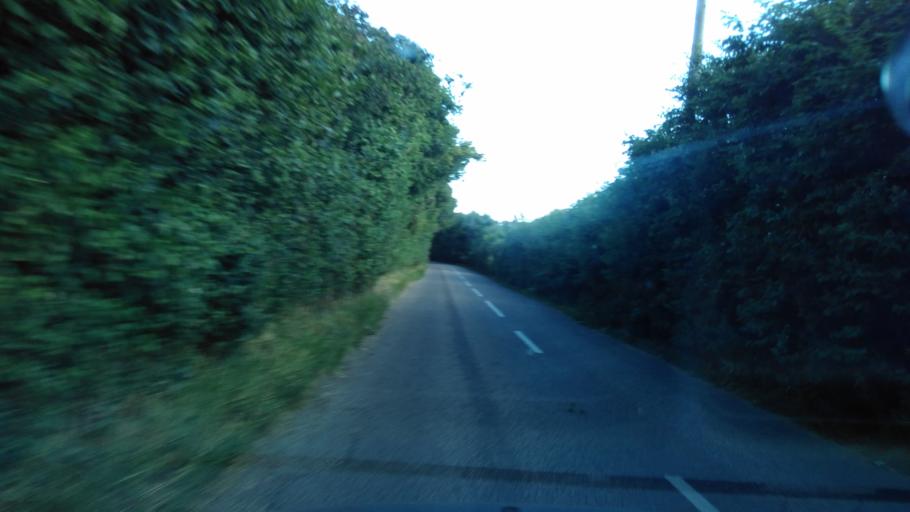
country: GB
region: England
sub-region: Kent
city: Dunkirk
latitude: 51.2541
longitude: 0.9574
